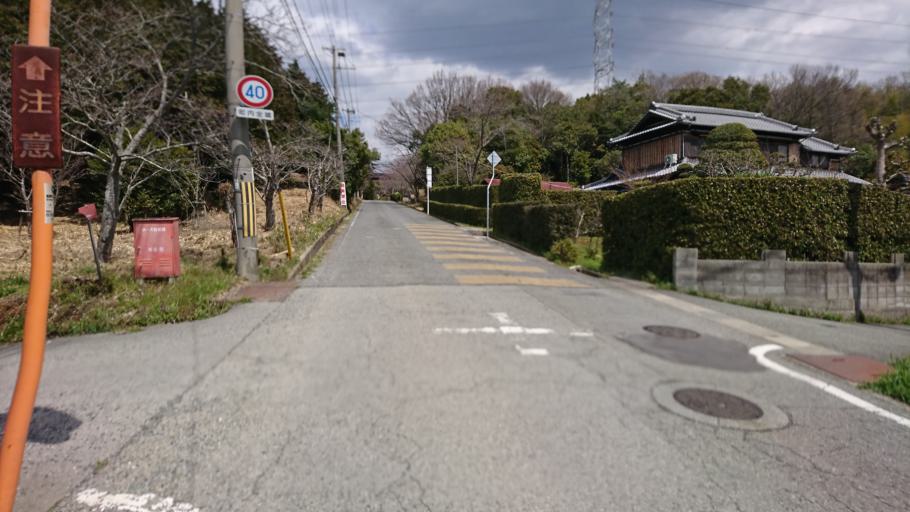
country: JP
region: Hyogo
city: Miki
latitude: 34.7713
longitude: 134.9475
